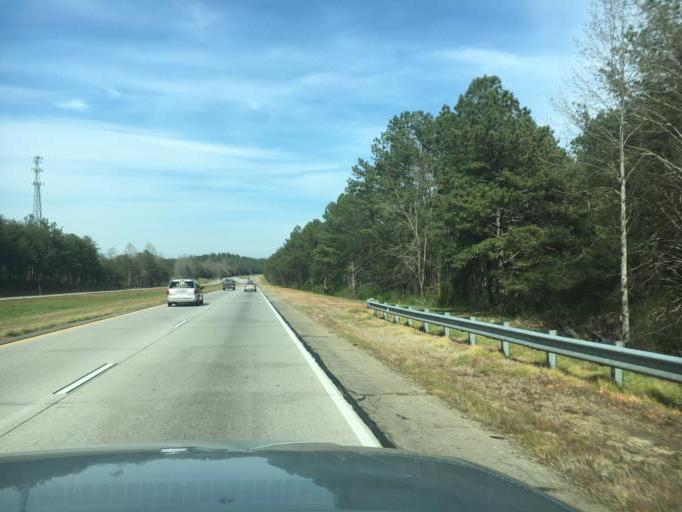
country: US
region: Georgia
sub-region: Hall County
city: Lula
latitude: 34.3704
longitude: -83.7299
